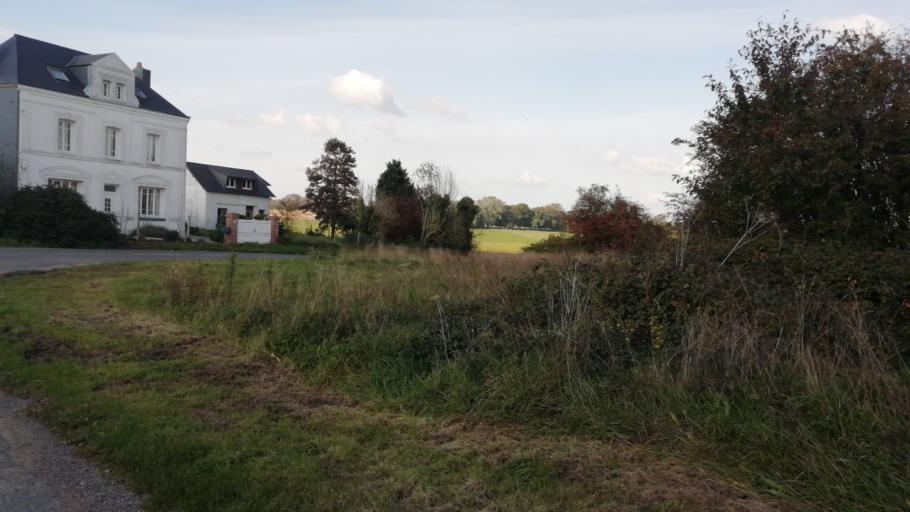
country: FR
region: Haute-Normandie
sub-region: Departement de la Seine-Maritime
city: Turretot
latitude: 49.6141
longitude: 0.2283
